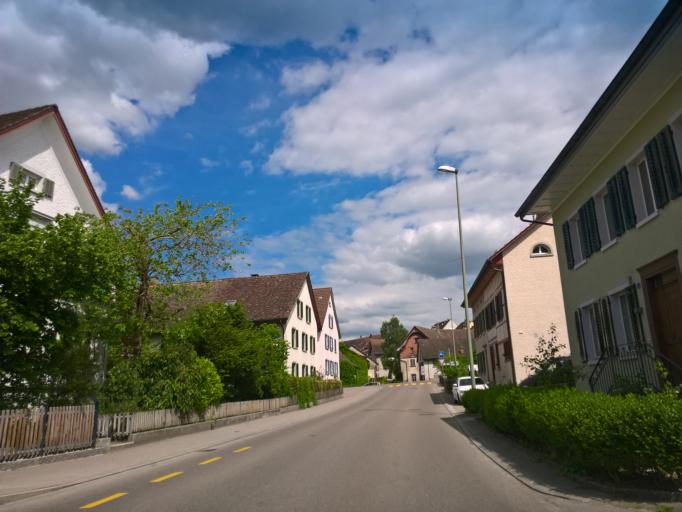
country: CH
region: Zurich
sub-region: Bezirk Andelfingen
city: Grossandelfingen
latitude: 47.5954
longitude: 8.6766
